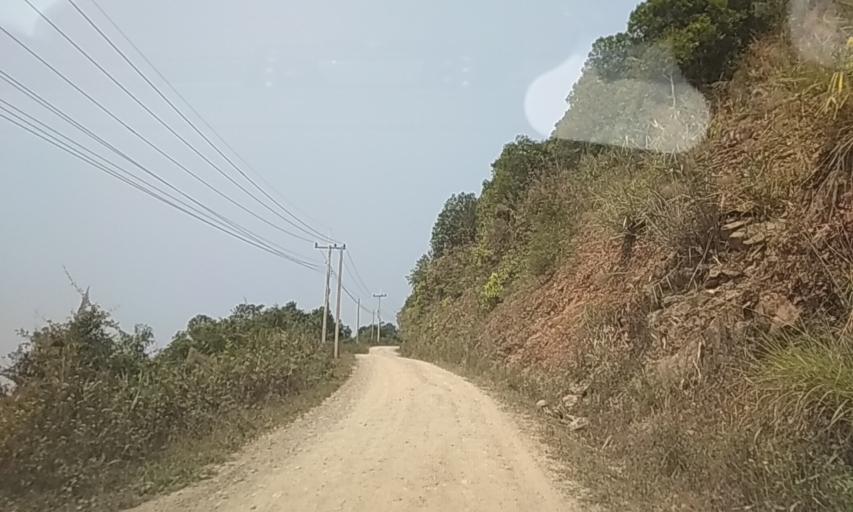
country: TH
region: Nan
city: Chaloem Phra Kiat
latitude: 20.0248
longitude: 101.0995
